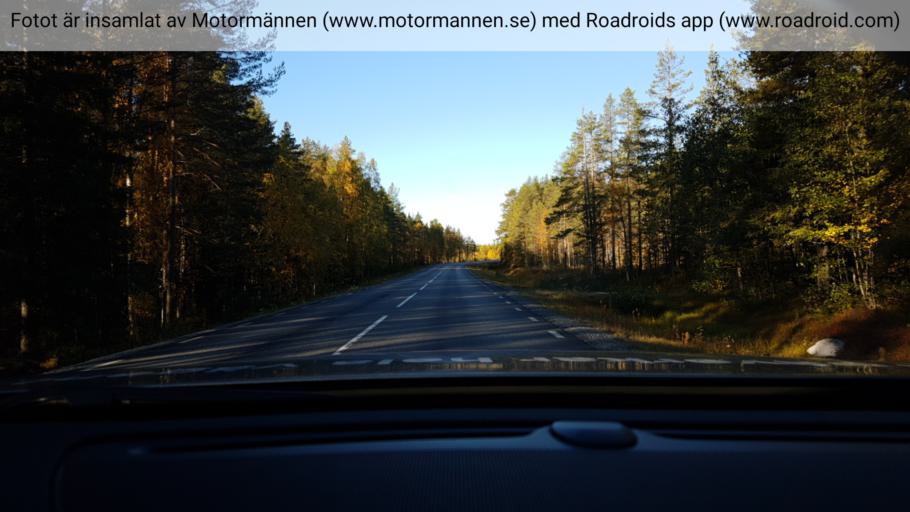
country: SE
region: Norrbotten
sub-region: Pitea Kommun
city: Roknas
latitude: 65.3422
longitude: 20.9747
